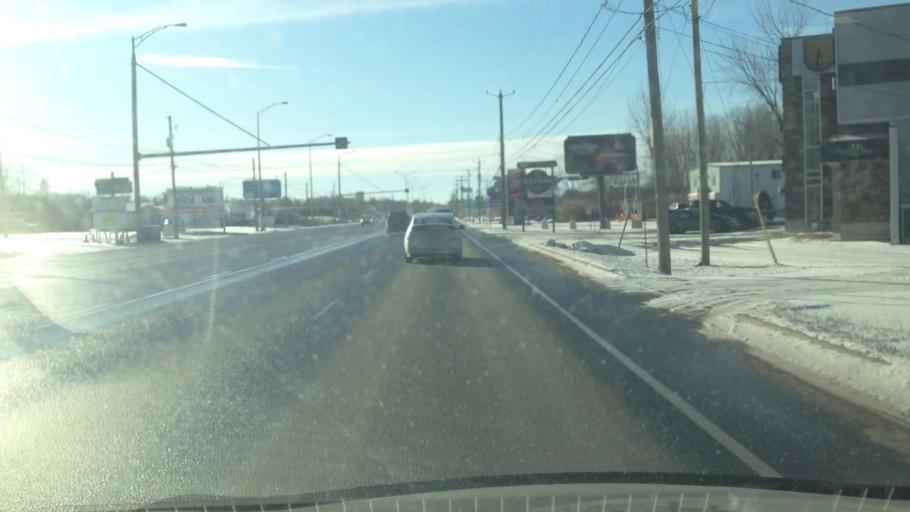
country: CA
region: Quebec
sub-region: Monteregie
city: Chateauguay
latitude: 45.3716
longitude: -73.7084
